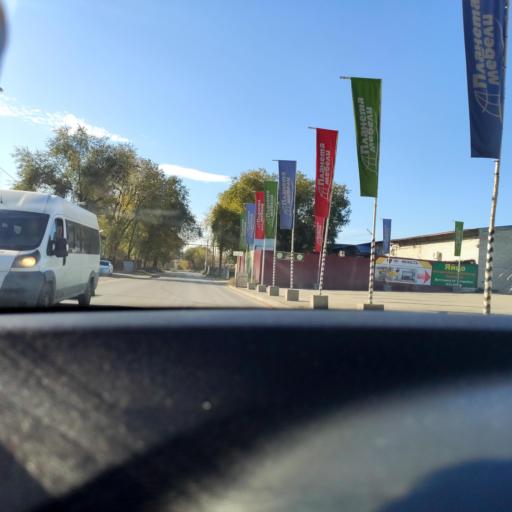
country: RU
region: Samara
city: Petra-Dubrava
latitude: 53.2449
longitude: 50.3006
